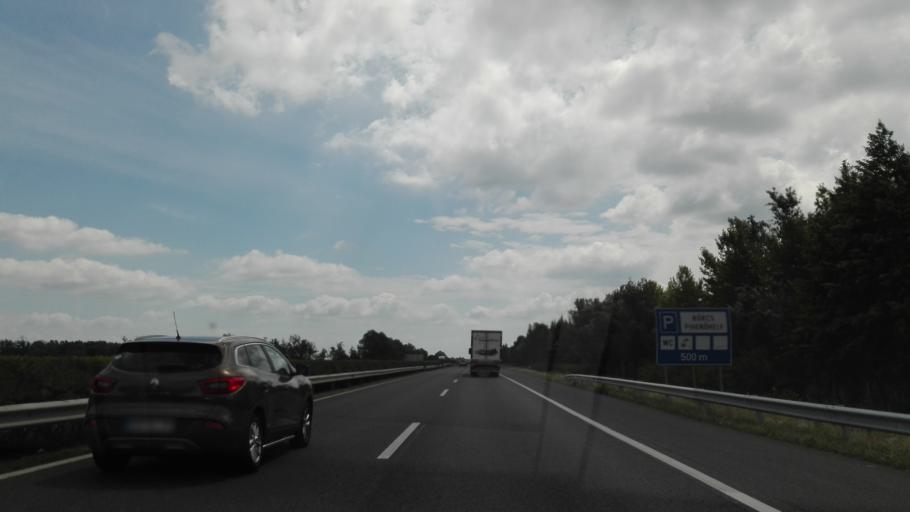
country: HU
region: Gyor-Moson-Sopron
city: Otteveny
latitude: 47.7125
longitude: 17.4771
